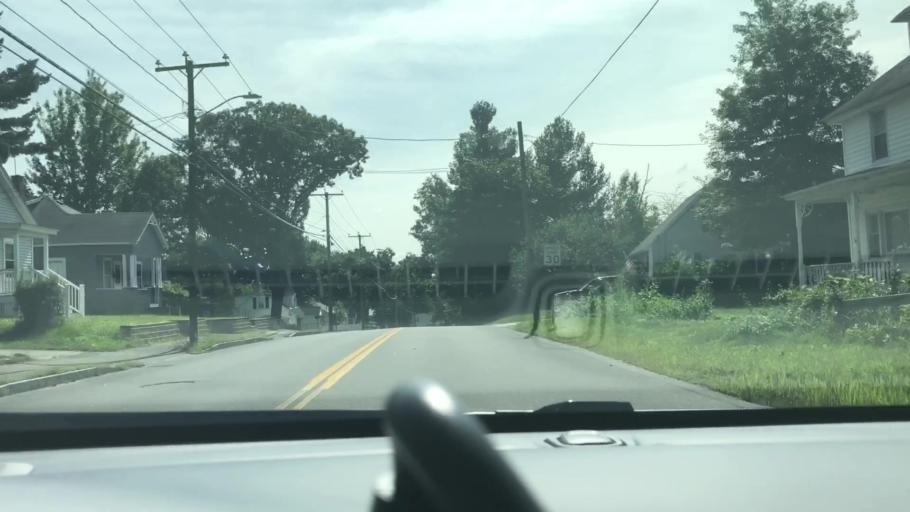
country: US
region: New Hampshire
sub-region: Hillsborough County
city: Pinardville
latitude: 42.9848
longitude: -71.4909
